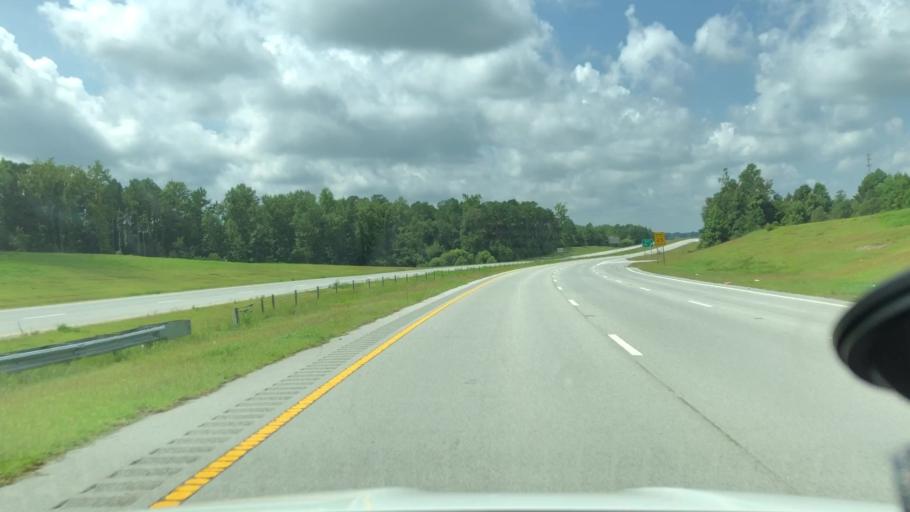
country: US
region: North Carolina
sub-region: Beaufort County
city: Washington
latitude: 35.5070
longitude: -77.0900
